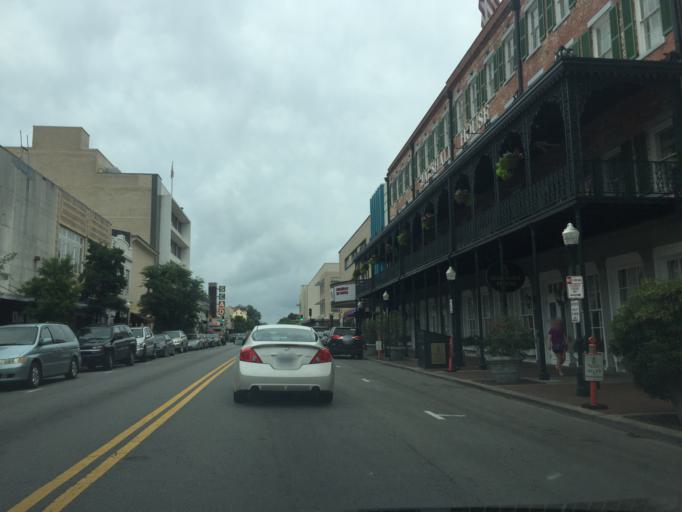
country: US
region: Georgia
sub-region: Chatham County
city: Savannah
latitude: 32.0786
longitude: -81.0907
